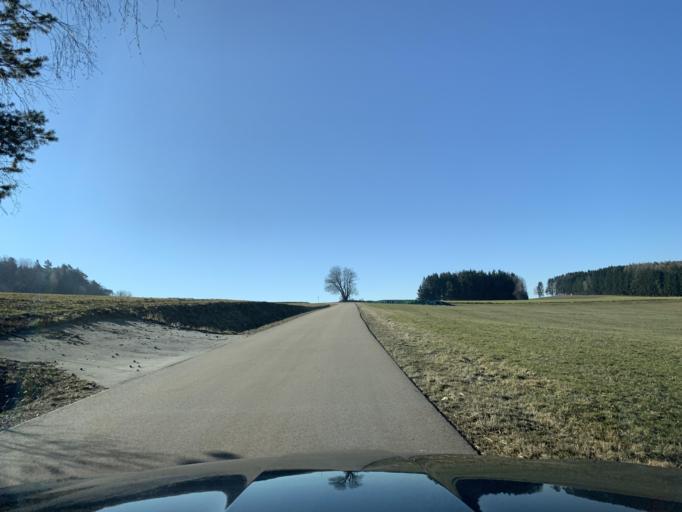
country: DE
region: Bavaria
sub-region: Upper Palatinate
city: Winklarn
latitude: 49.4189
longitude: 12.4488
